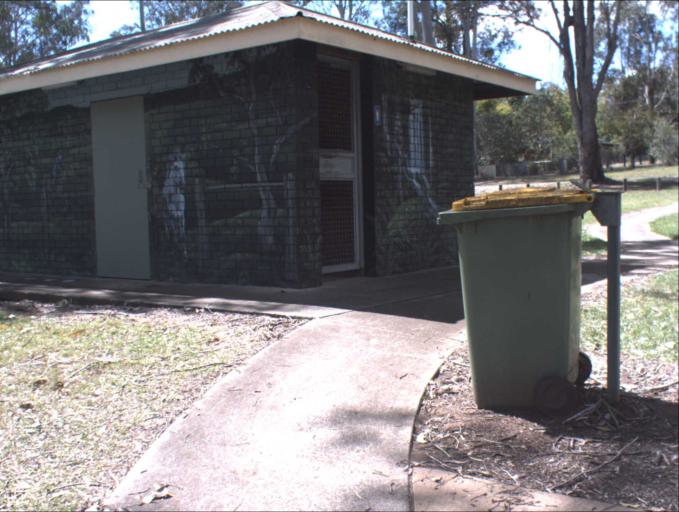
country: AU
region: Queensland
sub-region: Logan
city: Cedar Vale
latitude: -27.8595
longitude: 152.9788
